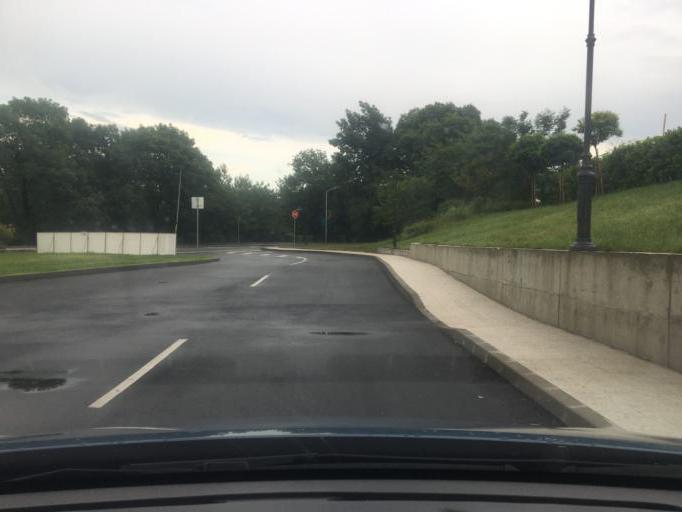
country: BG
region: Burgas
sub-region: Obshtina Burgas
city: Burgas
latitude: 42.5134
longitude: 27.4713
